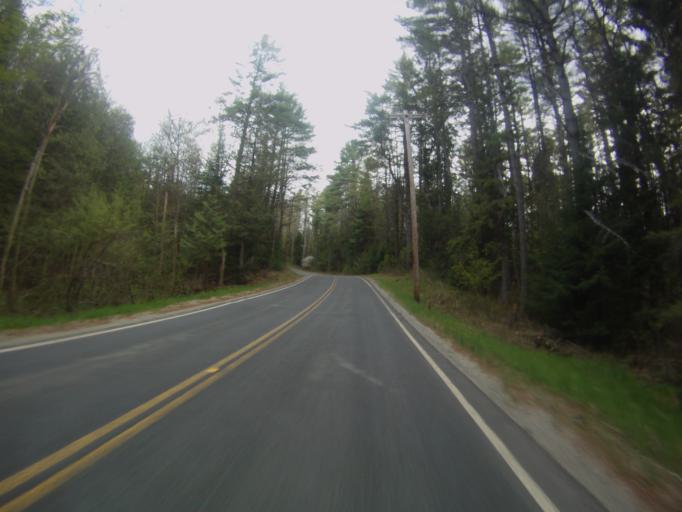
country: US
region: New York
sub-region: Warren County
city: Warrensburg
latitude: 43.8060
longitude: -73.9390
